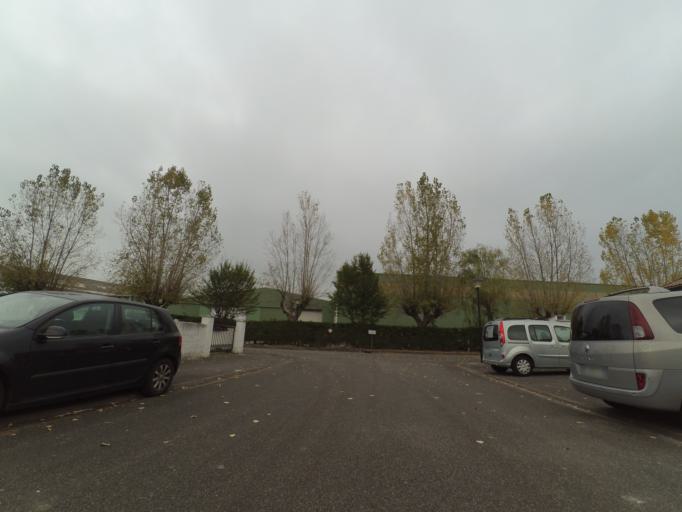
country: ES
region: Basque Country
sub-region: Provincia de Guipuzcoa
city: Irun
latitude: 43.3451
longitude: -1.7698
